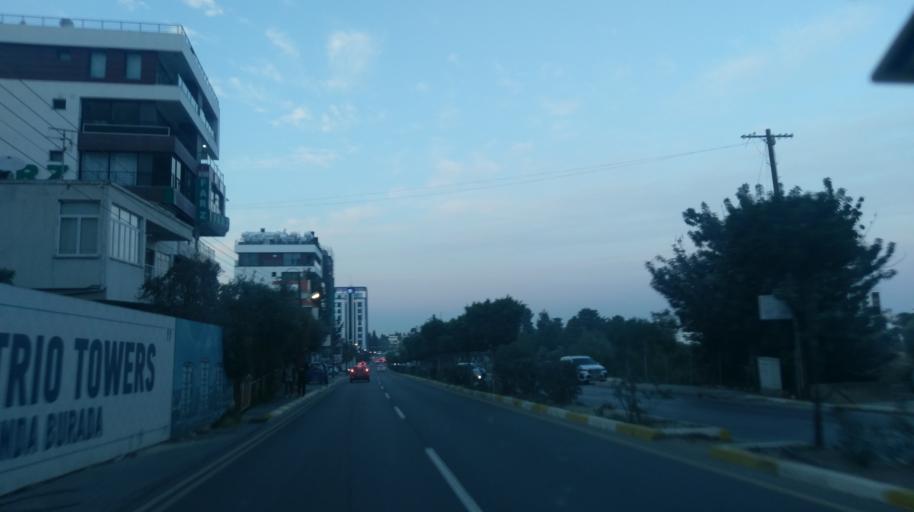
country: CY
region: Keryneia
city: Kyrenia
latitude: 35.3284
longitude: 33.3189
